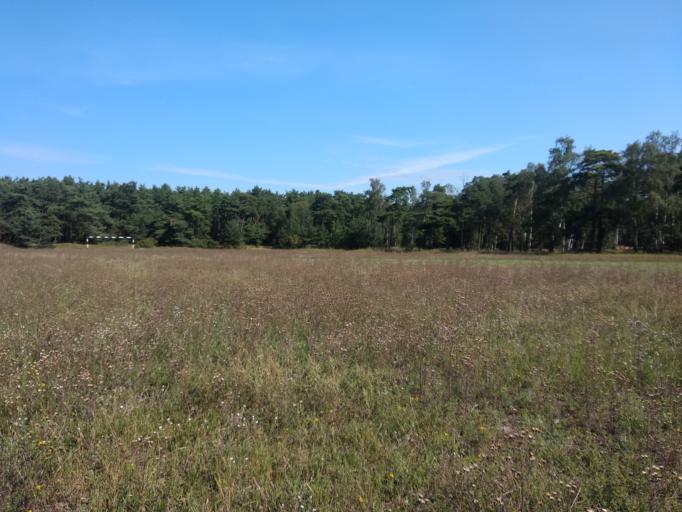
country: LT
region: Klaipedos apskritis
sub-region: Klaipeda
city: Klaipeda
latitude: 55.7276
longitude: 21.1105
